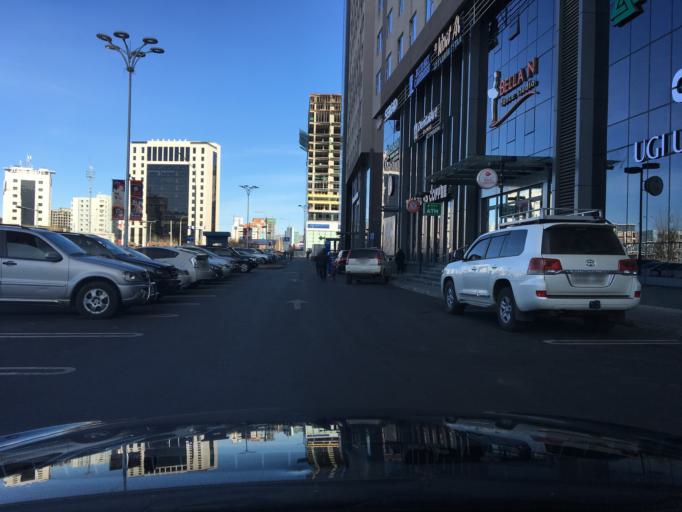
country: MN
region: Ulaanbaatar
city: Ulaanbaatar
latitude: 47.8980
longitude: 106.9089
